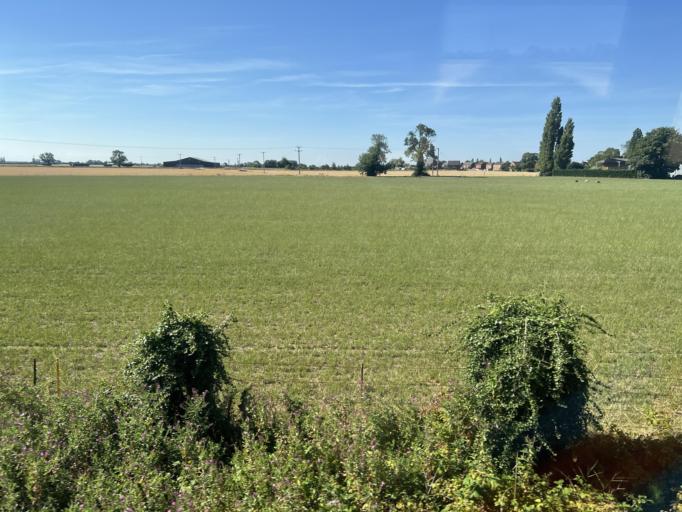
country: GB
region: England
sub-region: Lincolnshire
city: Heckington
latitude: 52.9753
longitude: -0.2831
